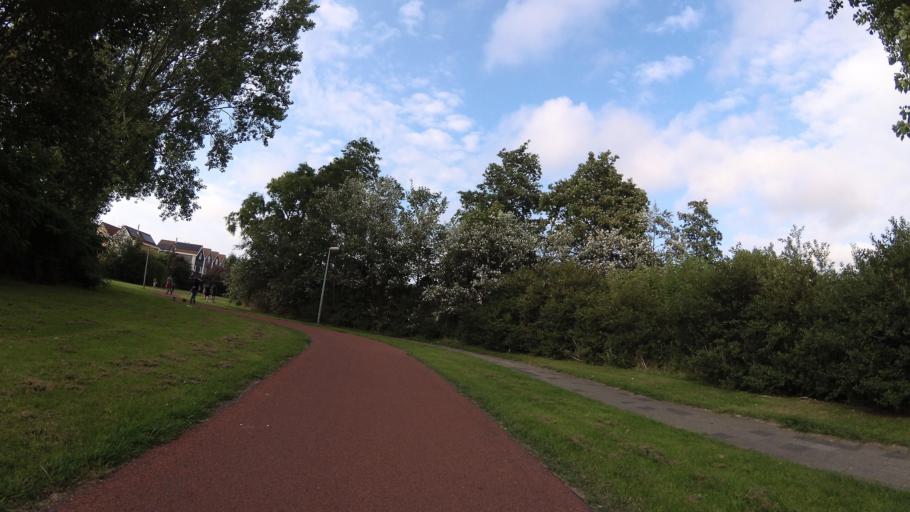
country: NL
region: North Holland
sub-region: Gemeente Den Helder
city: Den Helder
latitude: 52.8887
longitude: 4.7446
